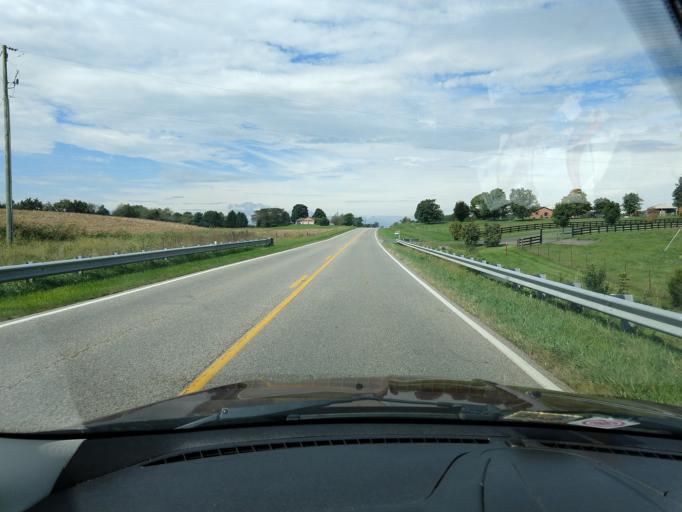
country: US
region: Virginia
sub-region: Augusta County
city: Weyers Cave
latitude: 38.2693
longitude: -78.8763
